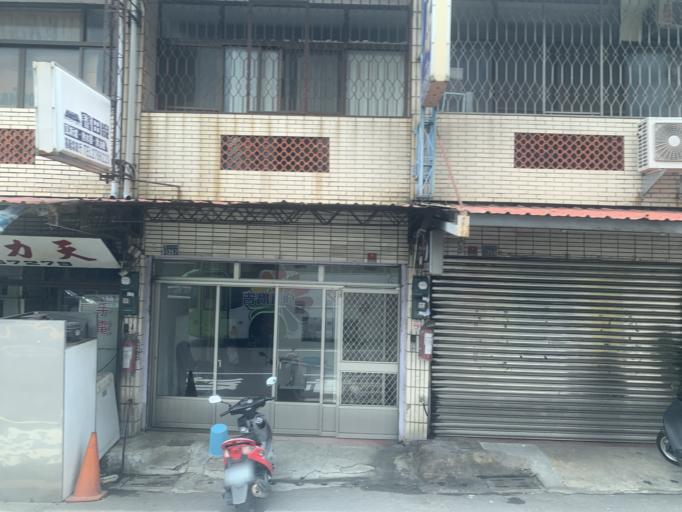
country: TW
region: Taiwan
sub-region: Chiayi
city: Jiayi Shi
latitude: 23.4921
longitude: 120.4715
